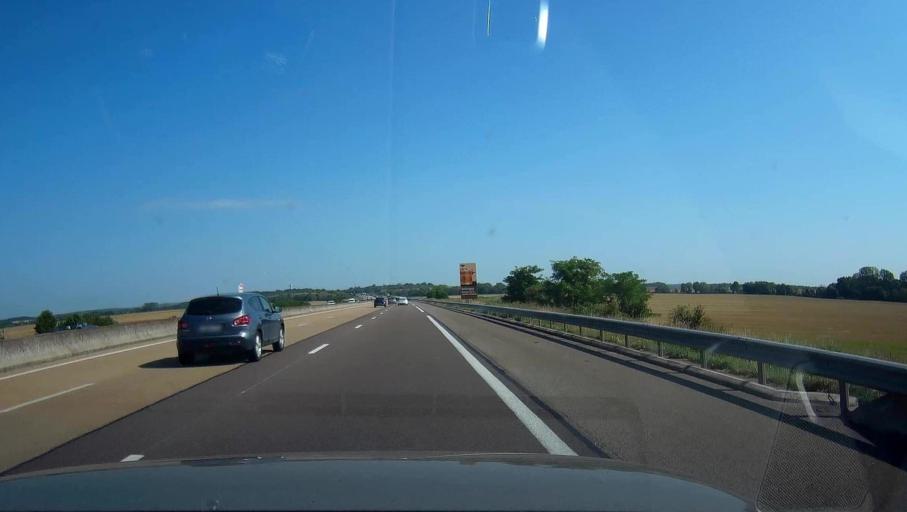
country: FR
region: Bourgogne
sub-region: Departement de la Cote-d'Or
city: Marcilly-sur-Tille
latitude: 47.5048
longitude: 5.1928
